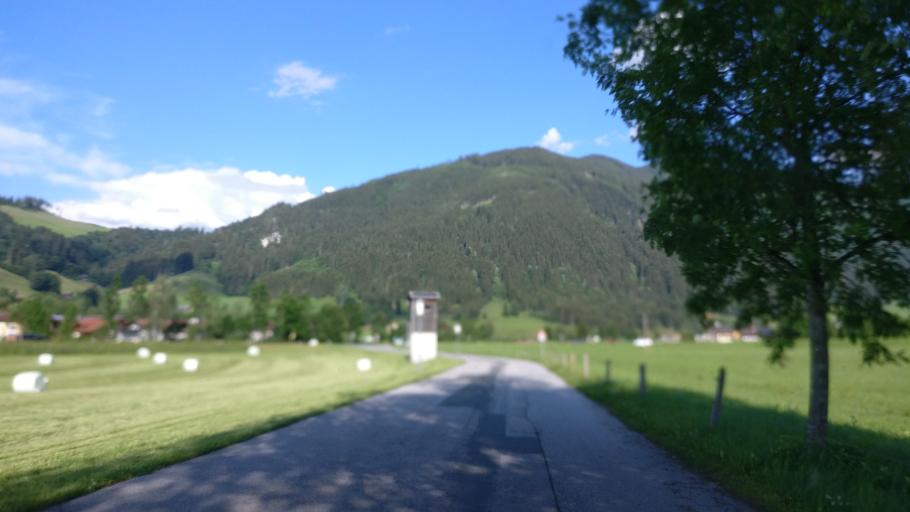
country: AT
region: Salzburg
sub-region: Politischer Bezirk Sankt Johann im Pongau
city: Radstadt
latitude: 47.3686
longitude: 13.4796
